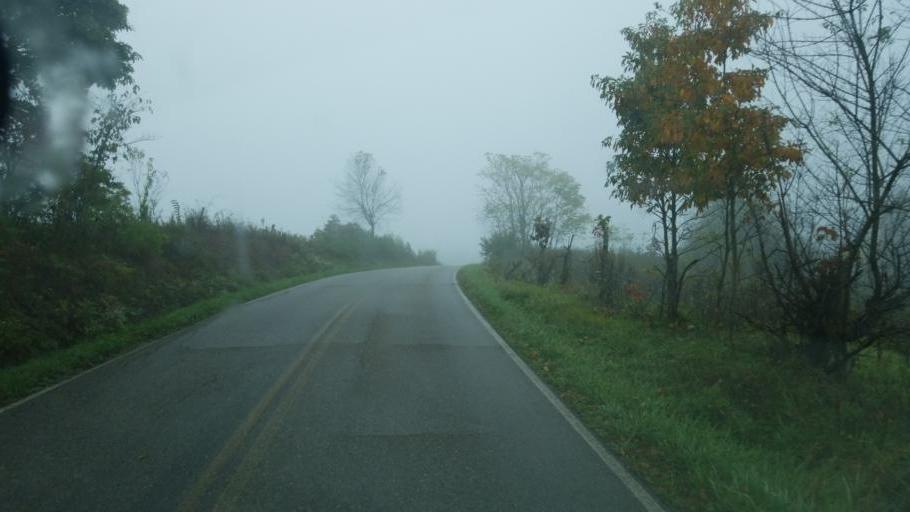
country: US
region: Ohio
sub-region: Harrison County
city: Cadiz
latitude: 40.3835
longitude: -81.1097
